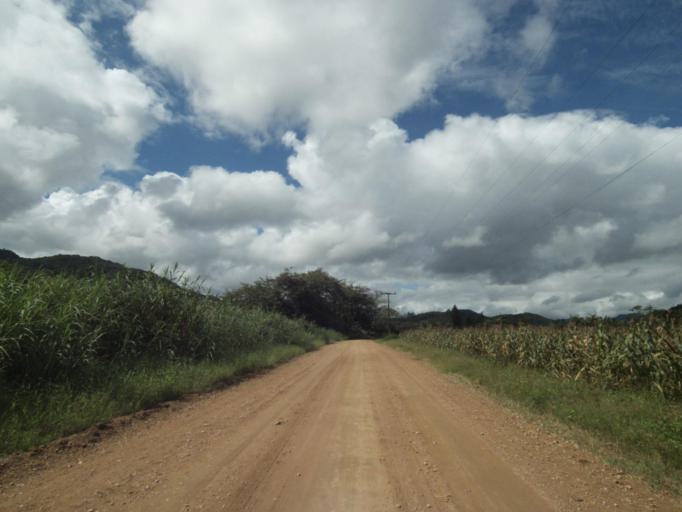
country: BR
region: Santa Catarina
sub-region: Pomerode
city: Pomerode
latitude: -26.6813
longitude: -49.1813
